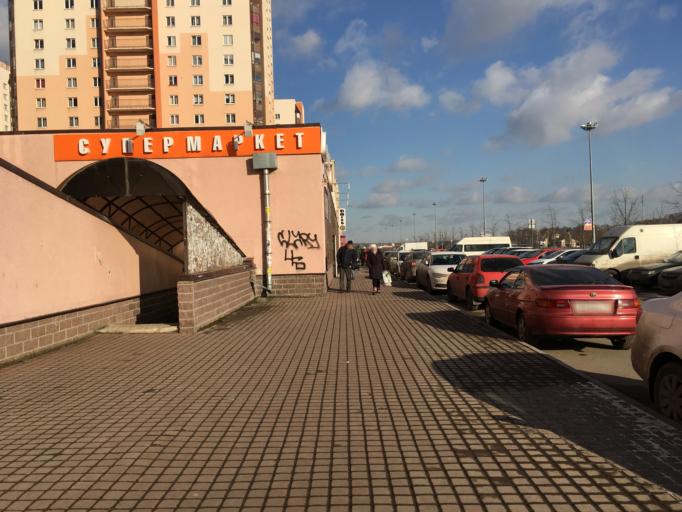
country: RU
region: St.-Petersburg
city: Krasnogvargeisky
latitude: 59.9132
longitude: 30.5088
